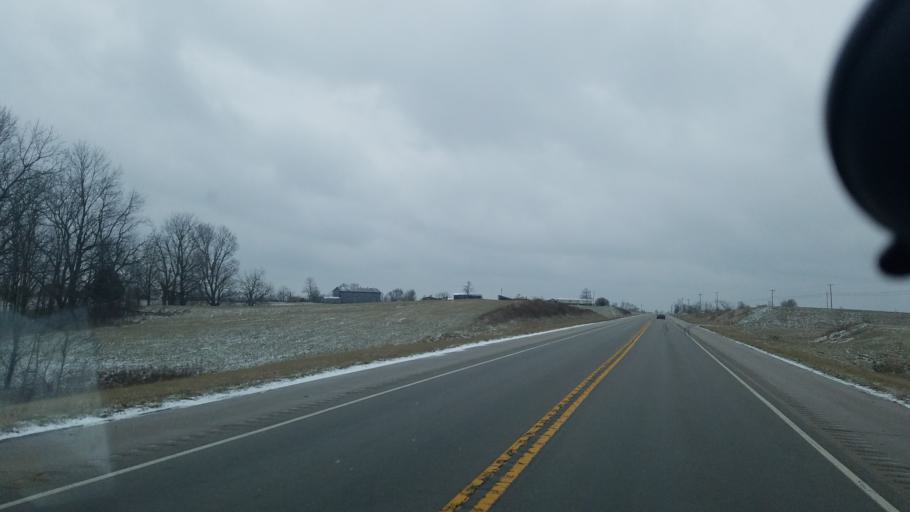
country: US
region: Kentucky
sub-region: Nicholas County
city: Carlisle
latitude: 38.2324
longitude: -83.9058
